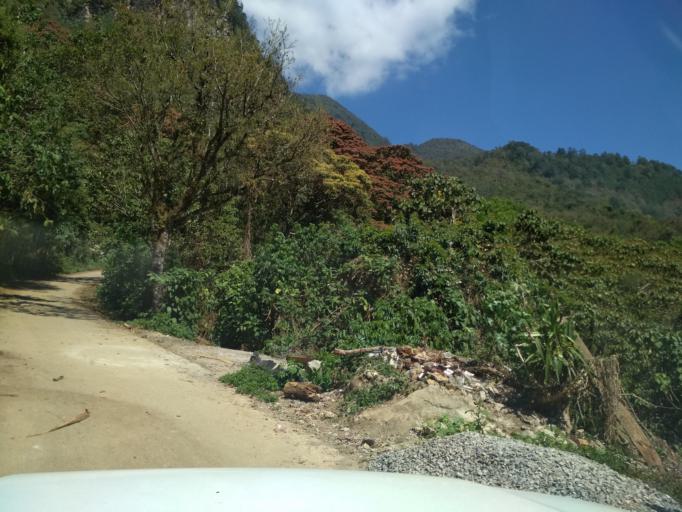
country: MX
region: Veracruz
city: Tequila
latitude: 18.7507
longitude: -97.0941
